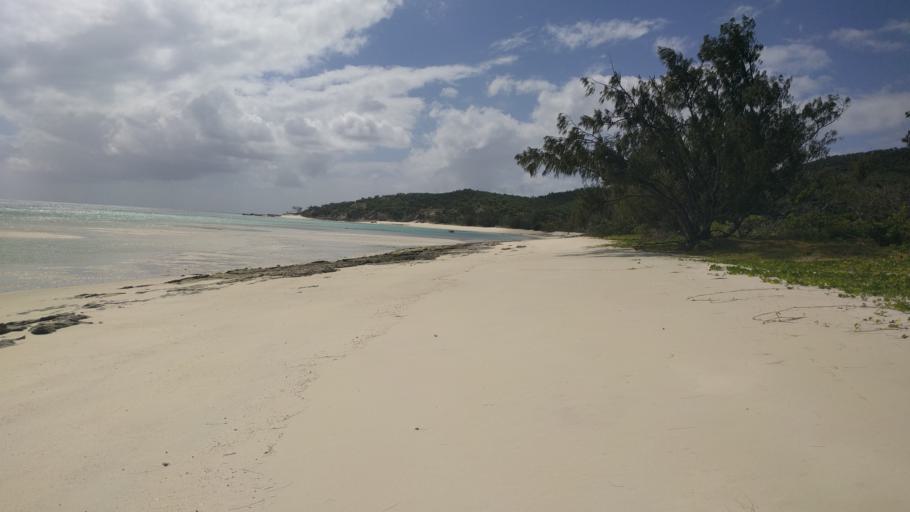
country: AU
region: Queensland
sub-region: Cook
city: Cooktown
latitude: -14.6785
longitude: 145.4473
